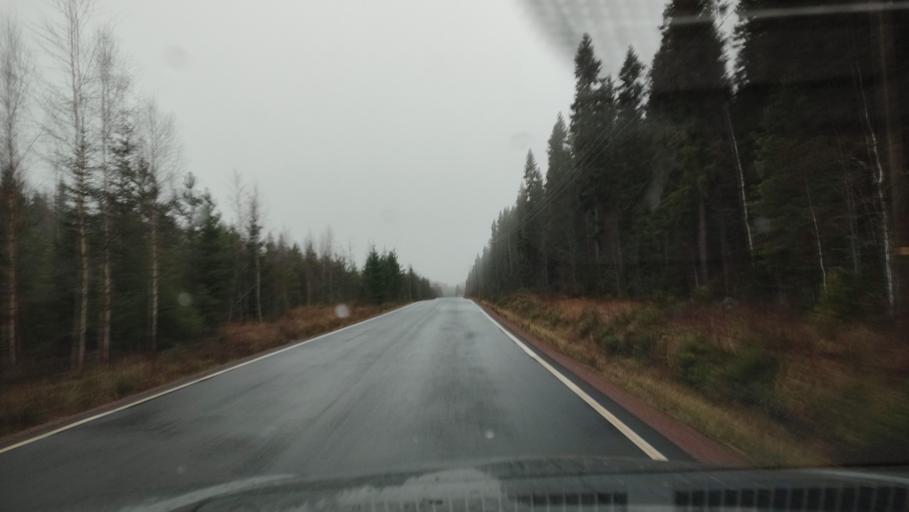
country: FI
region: Southern Ostrobothnia
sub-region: Suupohja
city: Karijoki
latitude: 62.1525
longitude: 21.7086
